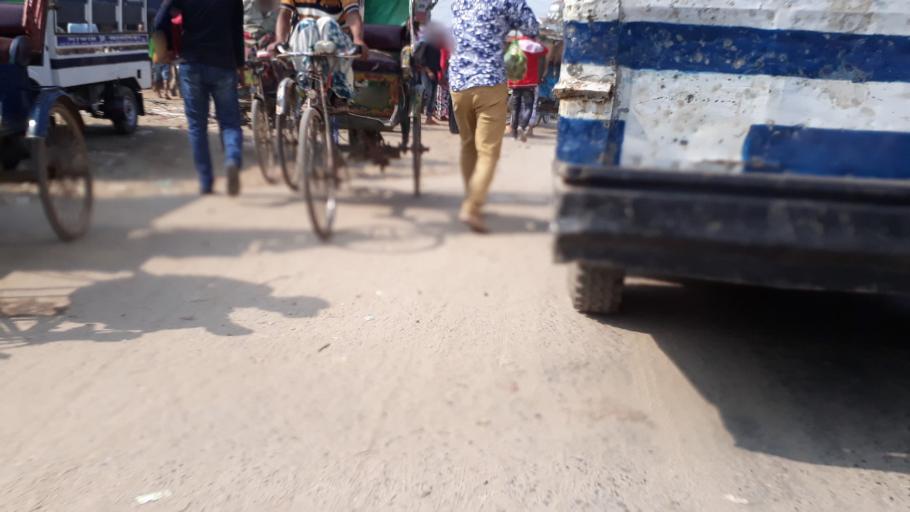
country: BD
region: Dhaka
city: Tungi
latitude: 23.8975
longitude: 90.3312
